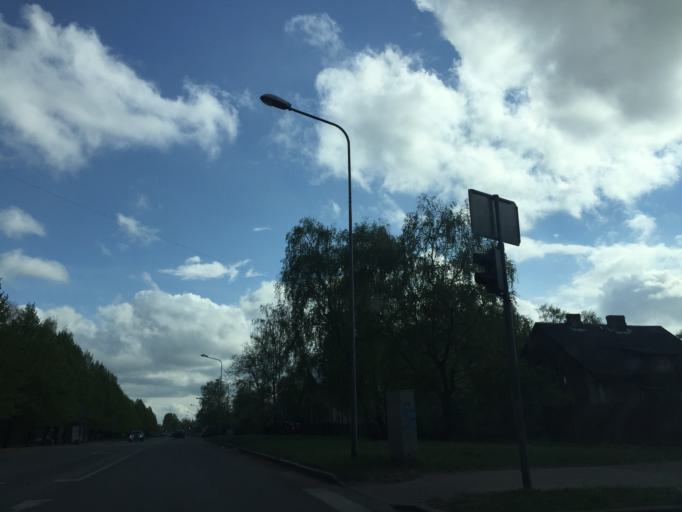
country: LV
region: Riga
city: Riga
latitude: 56.9458
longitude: 24.1957
